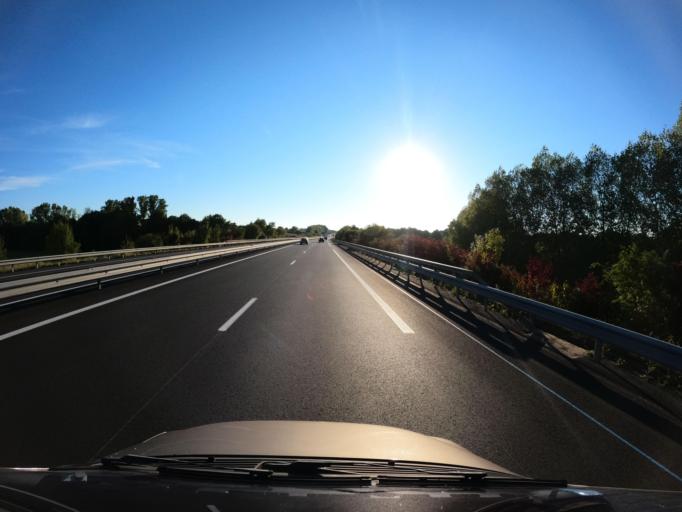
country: FR
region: Pays de la Loire
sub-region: Departement de la Vendee
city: Vendrennes
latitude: 46.8728
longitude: -1.1195
